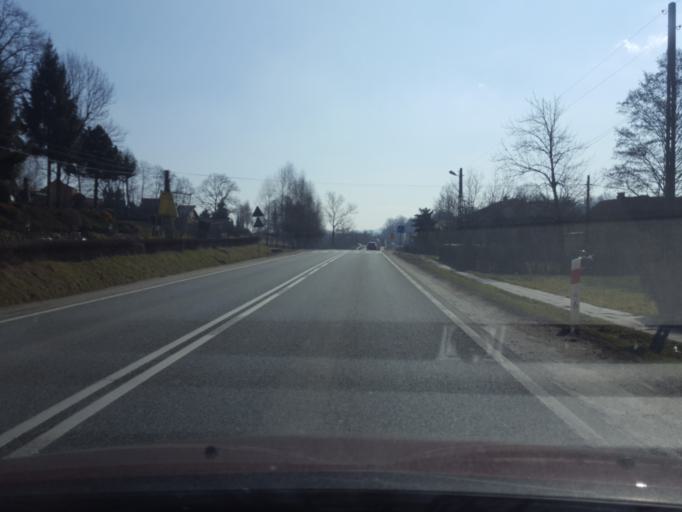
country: PL
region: Lesser Poland Voivodeship
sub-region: Powiat brzeski
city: Czchow
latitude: 49.8527
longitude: 20.6700
